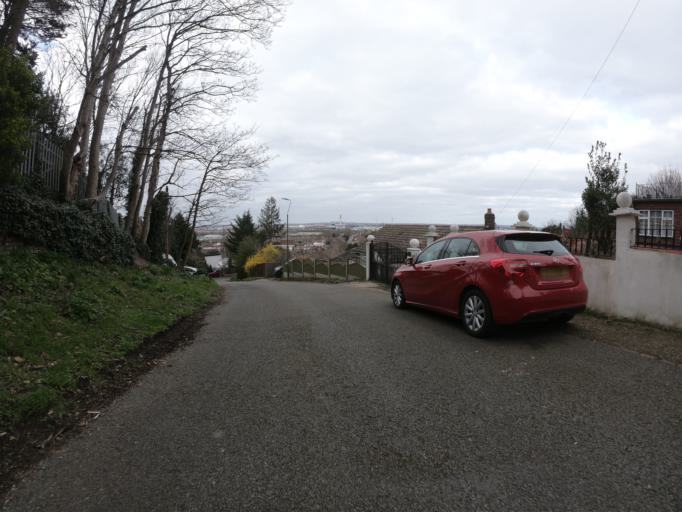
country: GB
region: England
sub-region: Greater London
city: Belvedere
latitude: 51.4881
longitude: 0.1506
